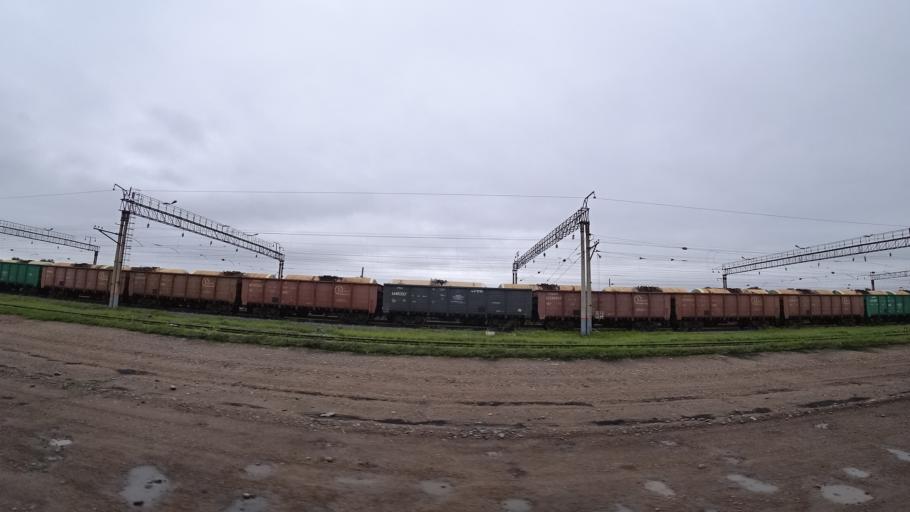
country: RU
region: Primorskiy
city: Chernigovka
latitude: 44.3393
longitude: 132.5315
